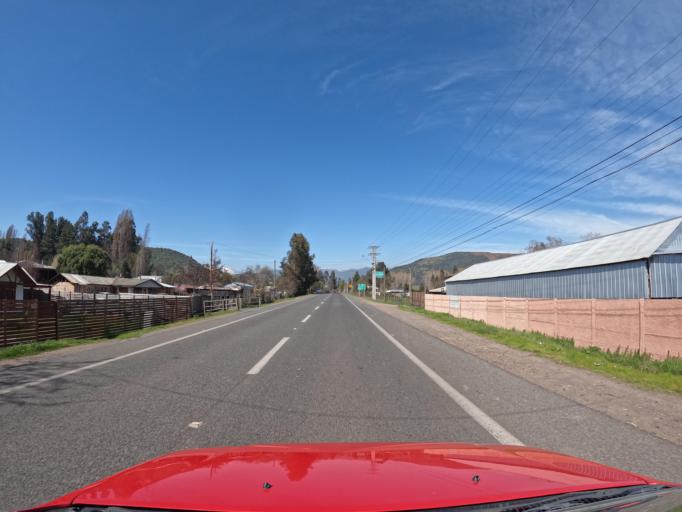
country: CL
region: Maule
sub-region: Provincia de Curico
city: Teno
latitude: -34.9776
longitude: -70.9947
